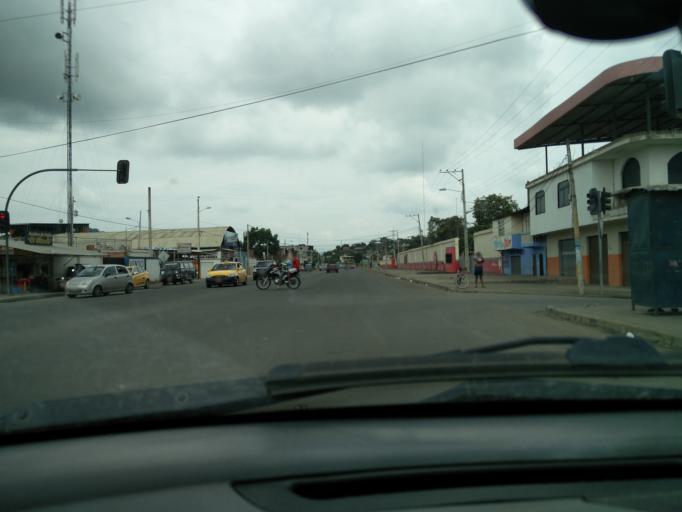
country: EC
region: Manabi
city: Portoviejo
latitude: -1.0725
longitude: -80.4450
